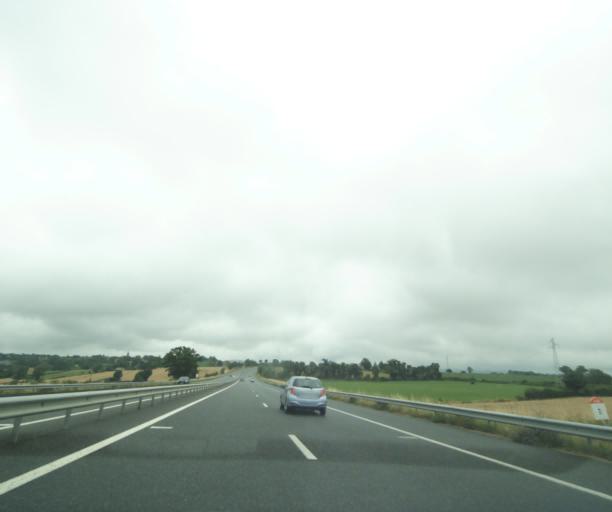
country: FR
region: Midi-Pyrenees
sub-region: Departement de l'Aveyron
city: Luc-la-Primaube
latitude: 44.3013
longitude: 2.5268
